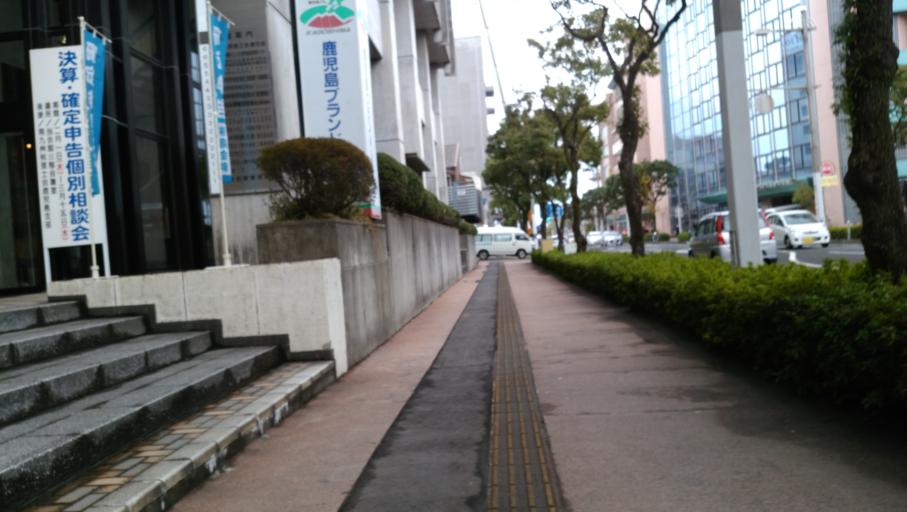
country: JP
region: Kagoshima
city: Kagoshima-shi
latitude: 31.5943
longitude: 130.5585
